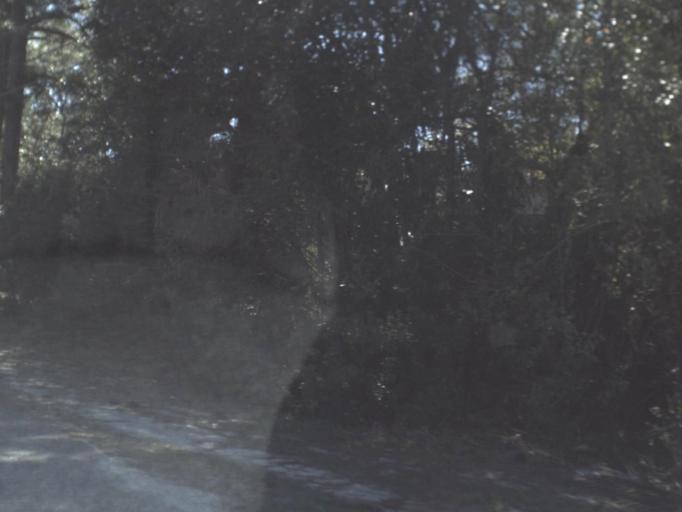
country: US
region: Florida
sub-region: Bay County
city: Panama City
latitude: 30.1791
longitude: -85.6638
